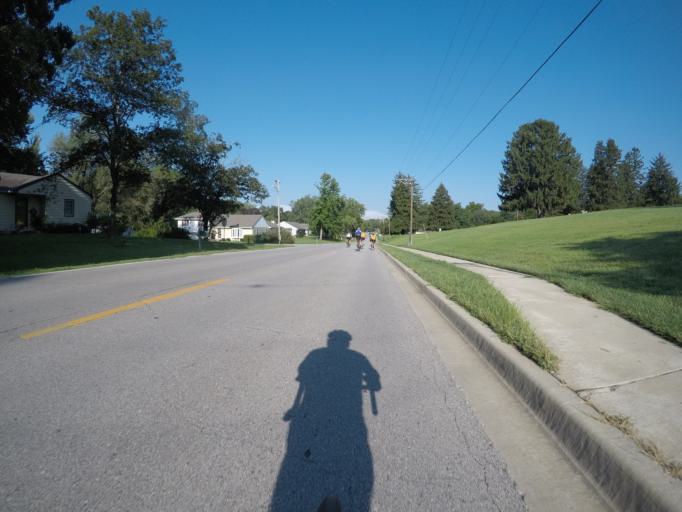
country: US
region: Missouri
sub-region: Platte County
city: Weston
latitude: 39.4106
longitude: -94.8900
